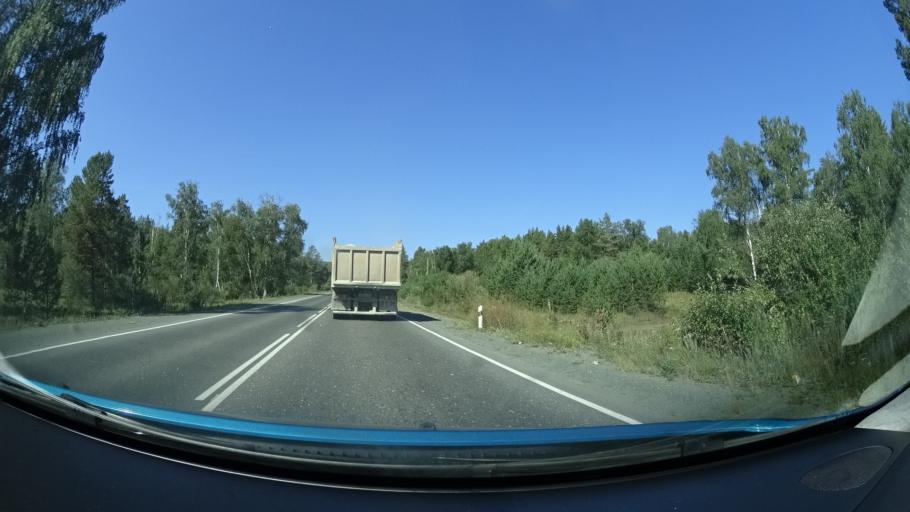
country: RU
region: Bashkortostan
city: Abzakovo
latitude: 53.8616
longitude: 58.5501
